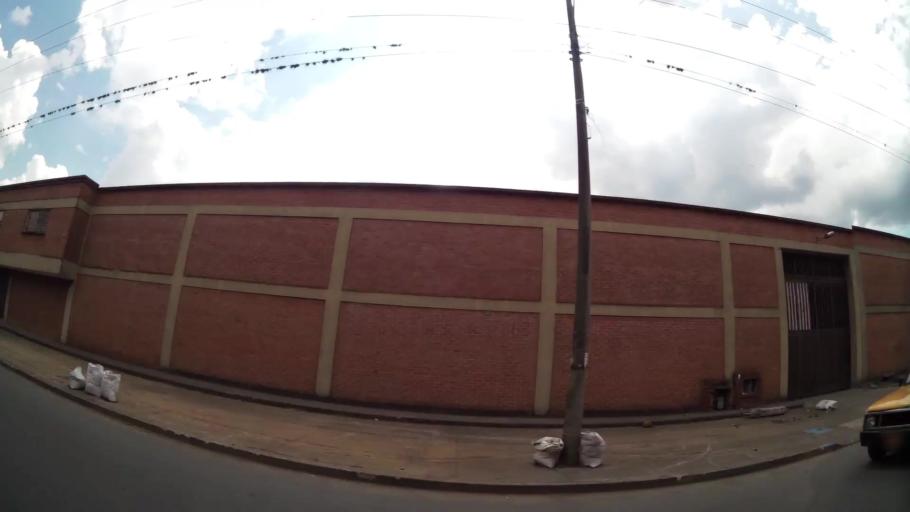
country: CO
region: Valle del Cauca
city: Cali
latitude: 3.4721
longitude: -76.5063
